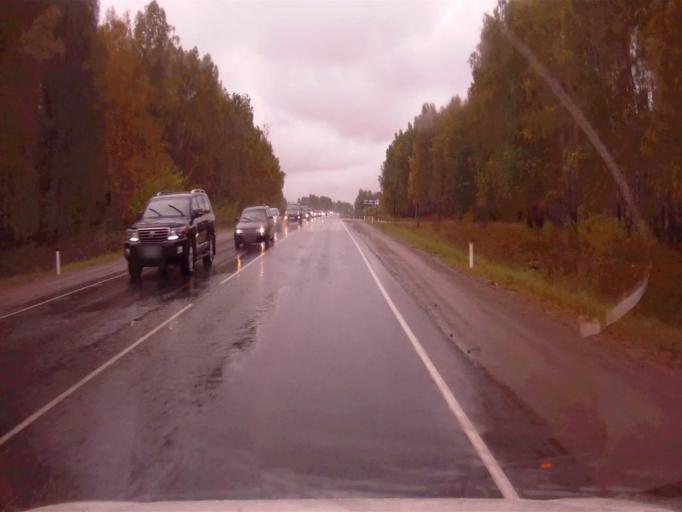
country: RU
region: Chelyabinsk
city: Argayash
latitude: 55.4668
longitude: 60.9093
